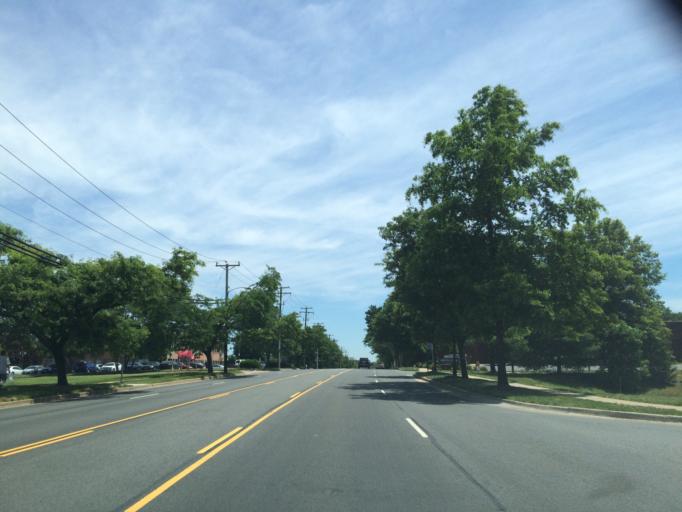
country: US
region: Virginia
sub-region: Fairfax County
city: Rose Hill
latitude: 38.8032
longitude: -77.1196
